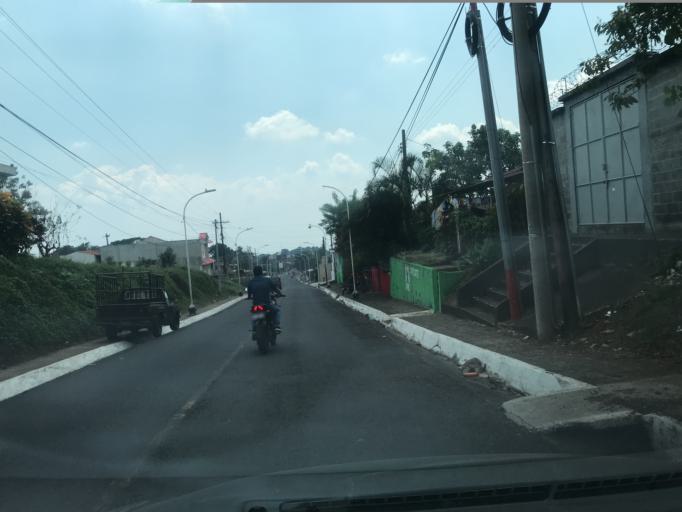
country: GT
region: Suchitepeque
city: San Francisco Zapotitlan
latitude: 14.5935
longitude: -91.5200
